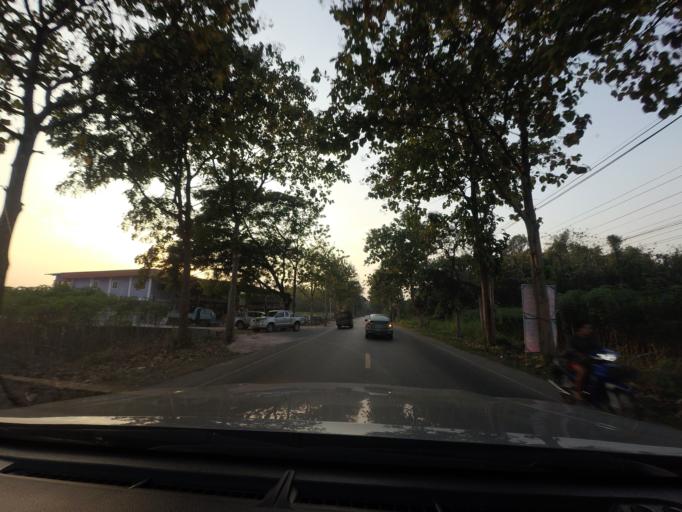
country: TH
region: Phitsanulok
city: Wang Thong
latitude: 16.7375
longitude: 100.4427
